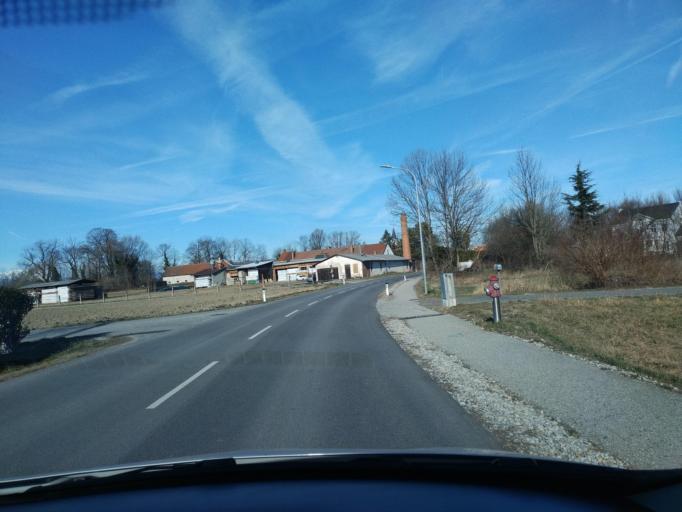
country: AT
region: Lower Austria
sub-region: Politischer Bezirk Wiener Neustadt
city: Lanzenkirchen
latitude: 47.7396
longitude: 16.2432
